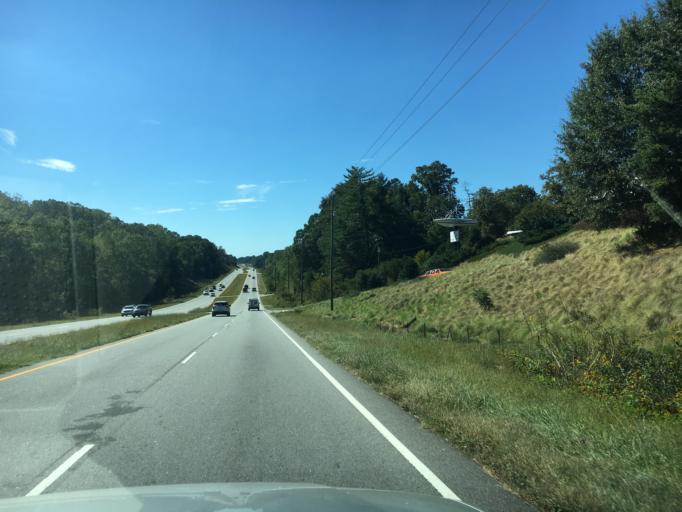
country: US
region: South Carolina
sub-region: Oconee County
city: Utica
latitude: 34.7028
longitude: -82.9104
